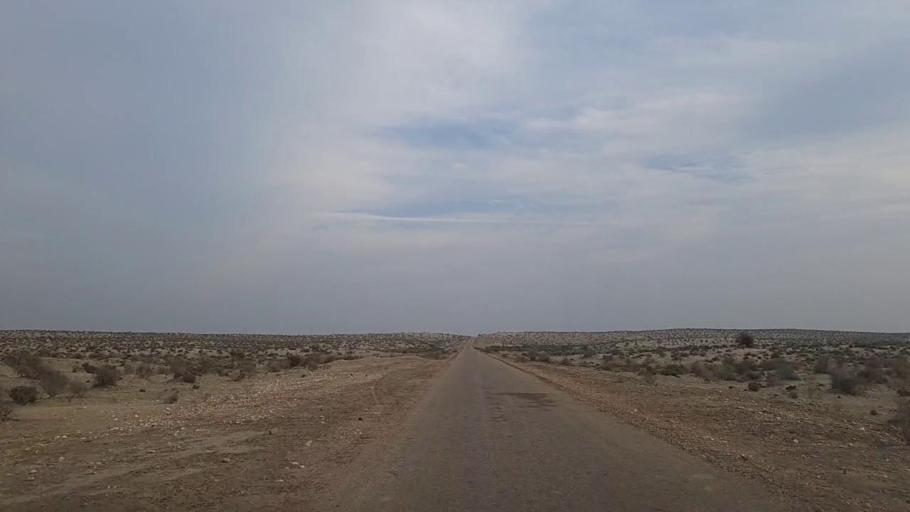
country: PK
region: Sindh
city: Daur
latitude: 26.5118
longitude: 68.5059
